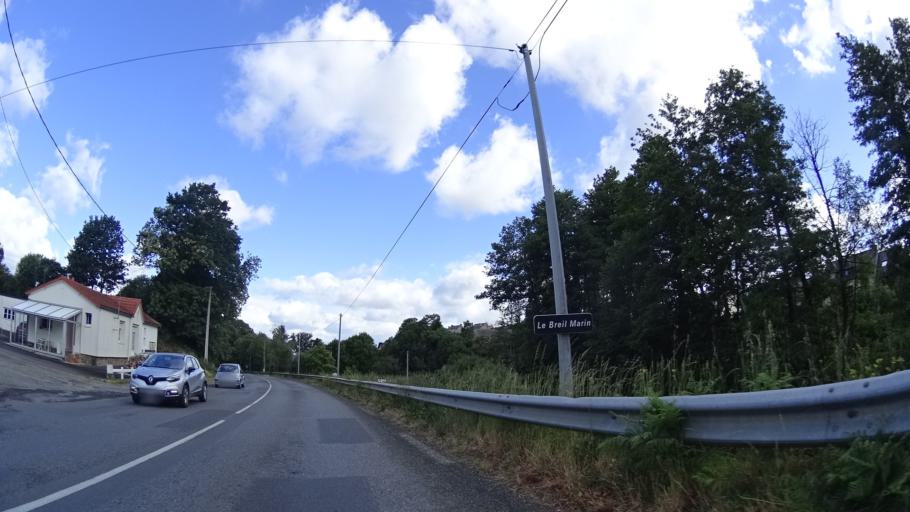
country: FR
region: Brittany
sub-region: Departement d'Ille-et-Vilaine
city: Hede-Bazouges
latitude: 48.2905
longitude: -1.8008
